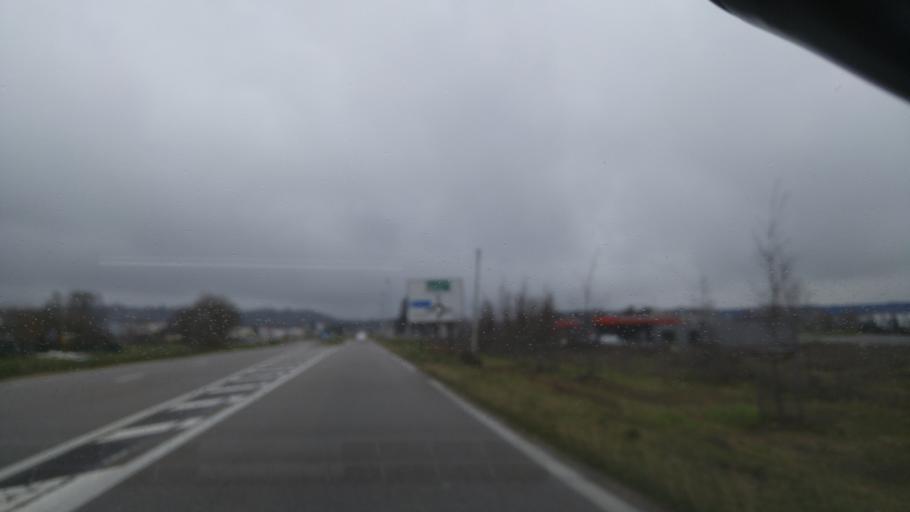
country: FR
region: Rhone-Alpes
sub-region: Departement de l'Isere
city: Grenay
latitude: 45.6589
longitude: 5.1057
